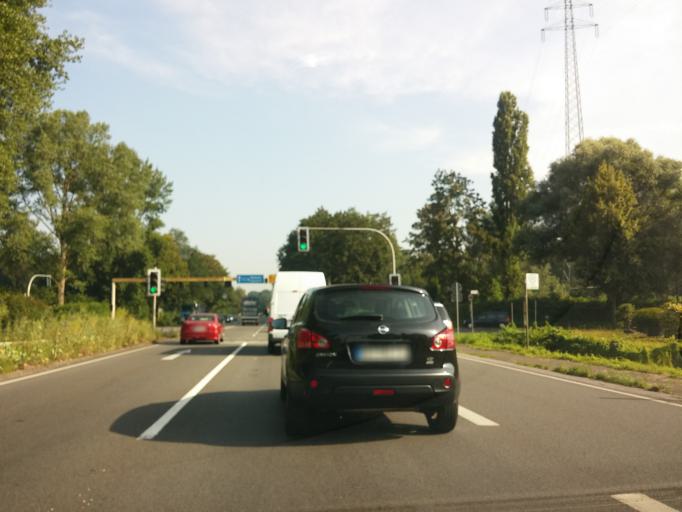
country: DE
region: North Rhine-Westphalia
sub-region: Regierungsbezirk Munster
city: Gladbeck
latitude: 51.5491
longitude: 6.9825
